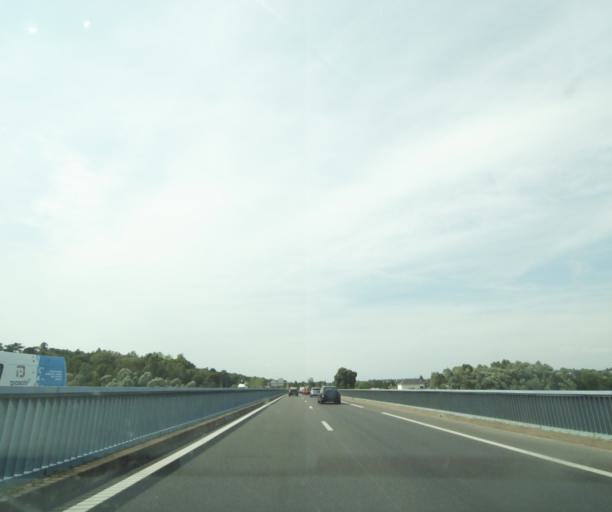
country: FR
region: Centre
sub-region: Departement d'Indre-et-Loire
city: Saint-Cyr-sur-Loire
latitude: 47.3913
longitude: 0.6480
